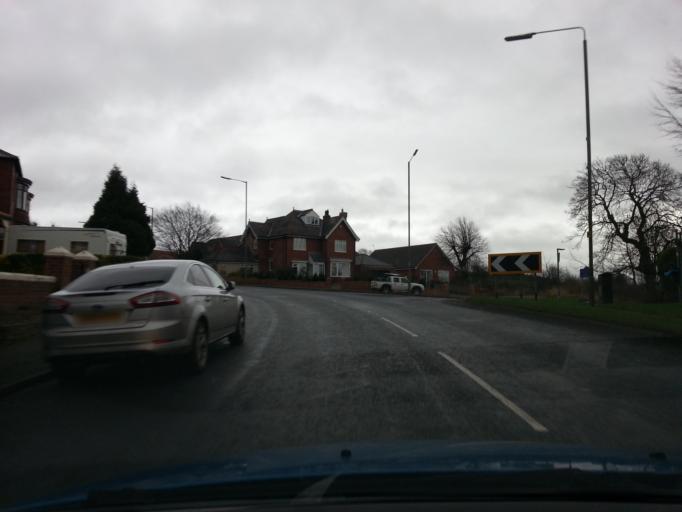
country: GB
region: England
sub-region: County Durham
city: Bishop Auckland
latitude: 54.6605
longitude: -1.6543
